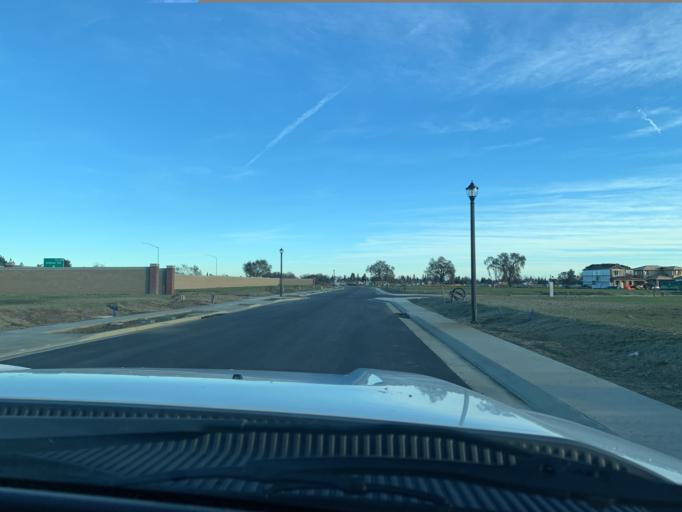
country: US
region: California
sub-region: Yolo County
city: Woodland
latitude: 38.6570
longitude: -121.7521
